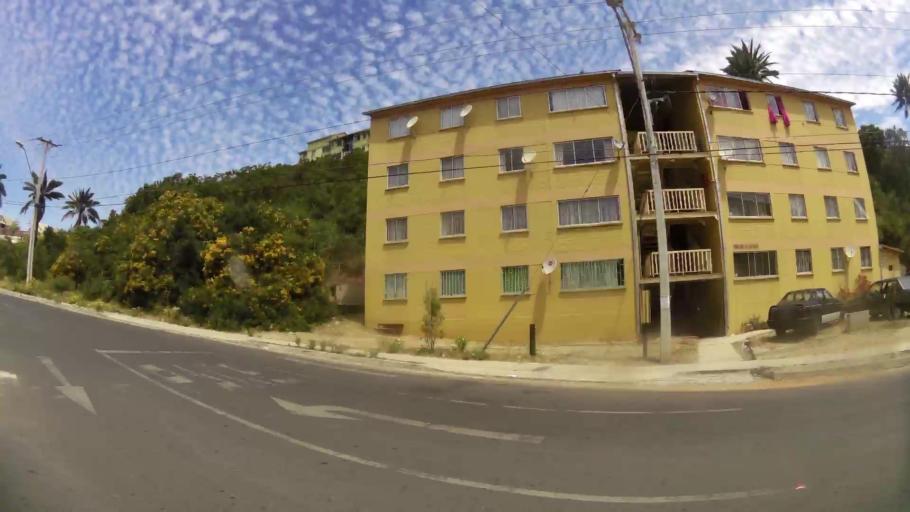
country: CL
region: Valparaiso
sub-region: Provincia de Valparaiso
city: Vina del Mar
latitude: -33.0603
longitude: -71.5601
